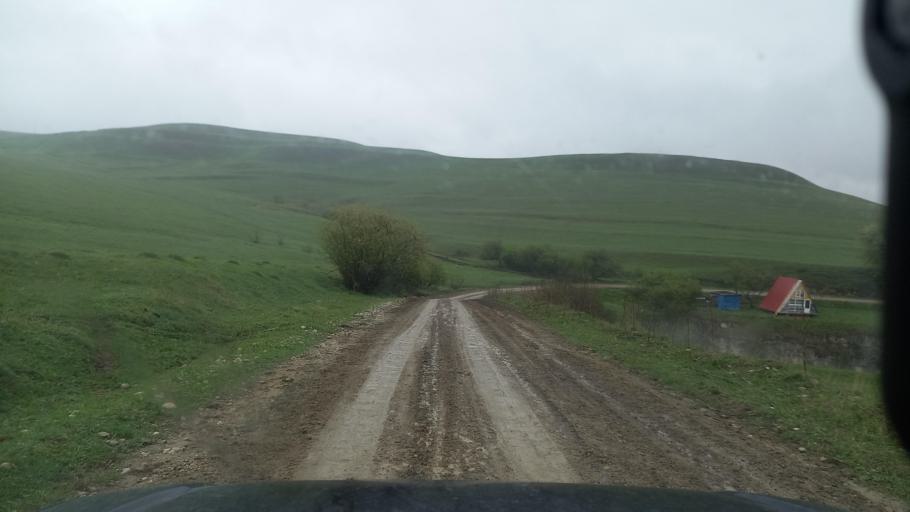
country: RU
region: Kabardino-Balkariya
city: Gundelen
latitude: 43.5938
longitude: 43.1228
